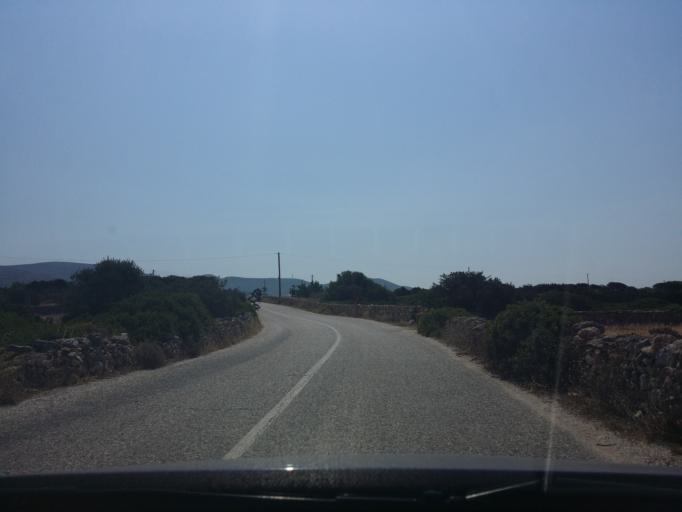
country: GR
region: South Aegean
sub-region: Nomos Kykladon
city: Antiparos
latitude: 37.0085
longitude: 25.1209
